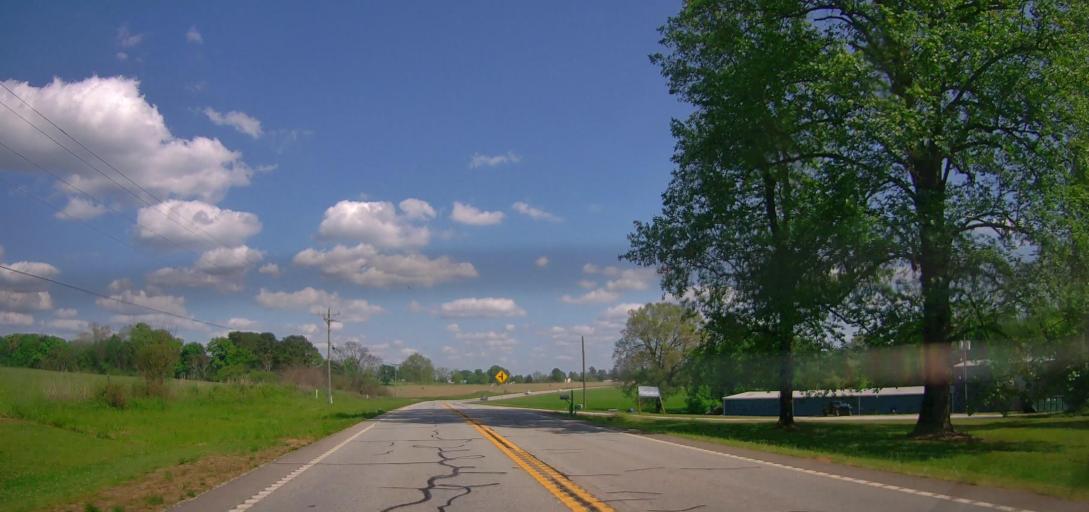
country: US
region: Georgia
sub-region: Greene County
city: Greensboro
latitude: 33.6129
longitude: -83.3152
